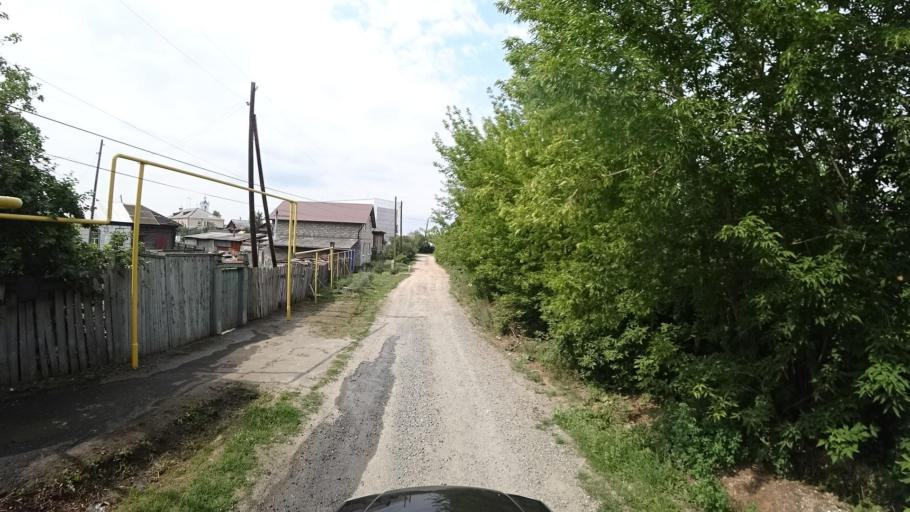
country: RU
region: Sverdlovsk
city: Kamyshlov
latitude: 56.8500
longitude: 62.6938
